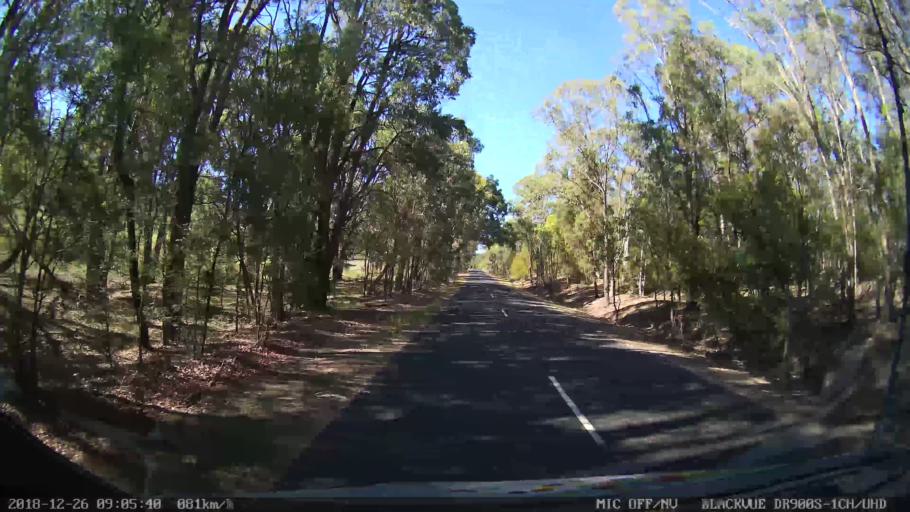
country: AU
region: New South Wales
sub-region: Mid-Western Regional
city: Kandos
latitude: -32.6852
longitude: 150.0062
